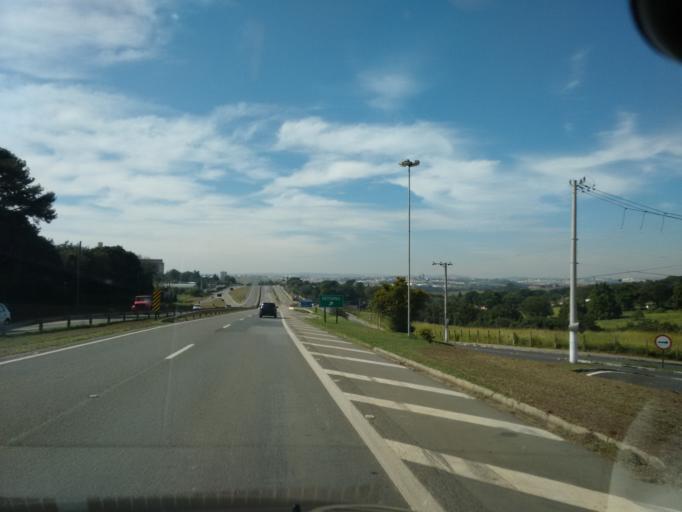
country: BR
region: Sao Paulo
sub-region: Itu
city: Itu
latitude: -23.2546
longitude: -47.3535
